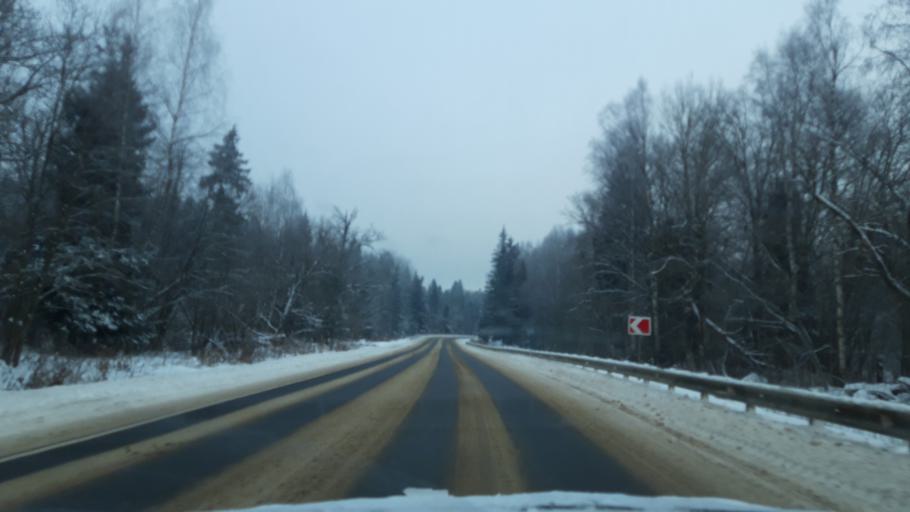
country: RU
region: Moskovskaya
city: Avtopoligon
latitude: 56.2806
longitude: 37.3750
